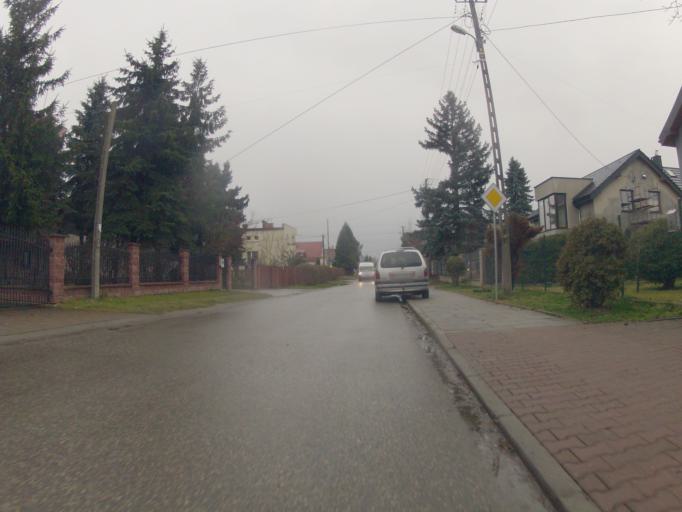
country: PL
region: Lesser Poland Voivodeship
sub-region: Powiat wielicki
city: Kokotow
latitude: 50.0566
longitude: 20.0455
